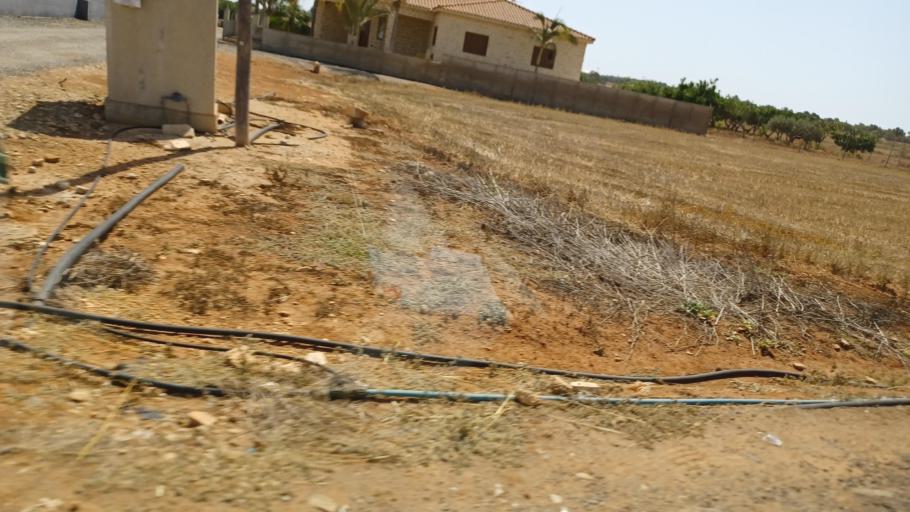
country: CY
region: Ammochostos
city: Paralimni
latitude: 35.0138
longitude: 33.9555
